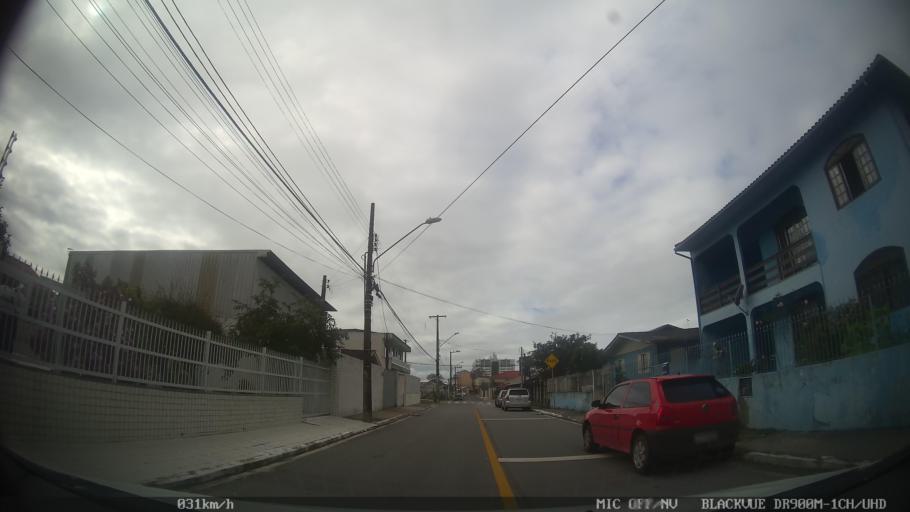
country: BR
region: Santa Catarina
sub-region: Sao Jose
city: Campinas
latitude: -27.5625
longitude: -48.6335
